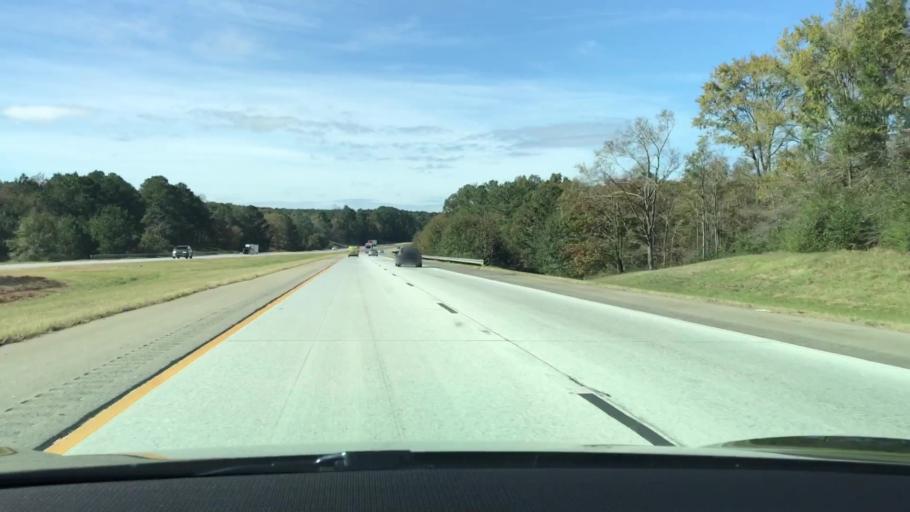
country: US
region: Georgia
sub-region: Greene County
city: Greensboro
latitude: 33.5375
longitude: -83.2399
